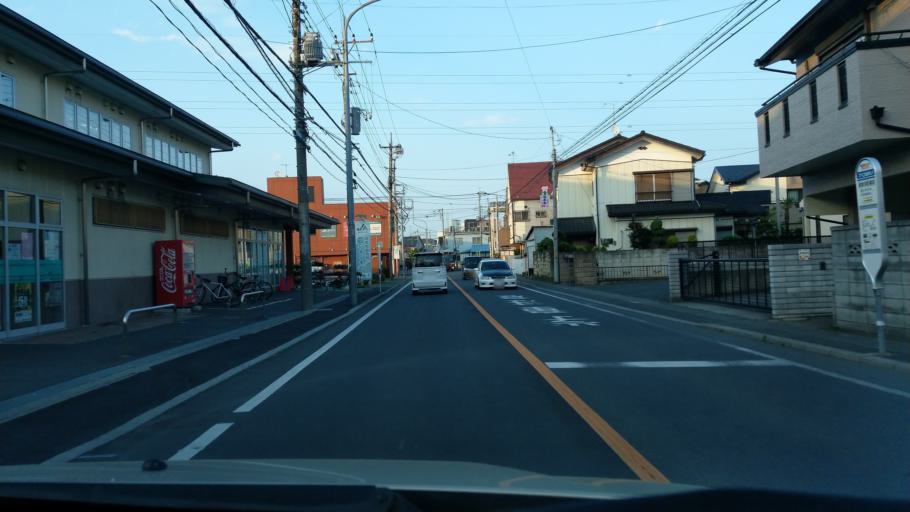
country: JP
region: Saitama
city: Yono
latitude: 35.8823
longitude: 139.6546
